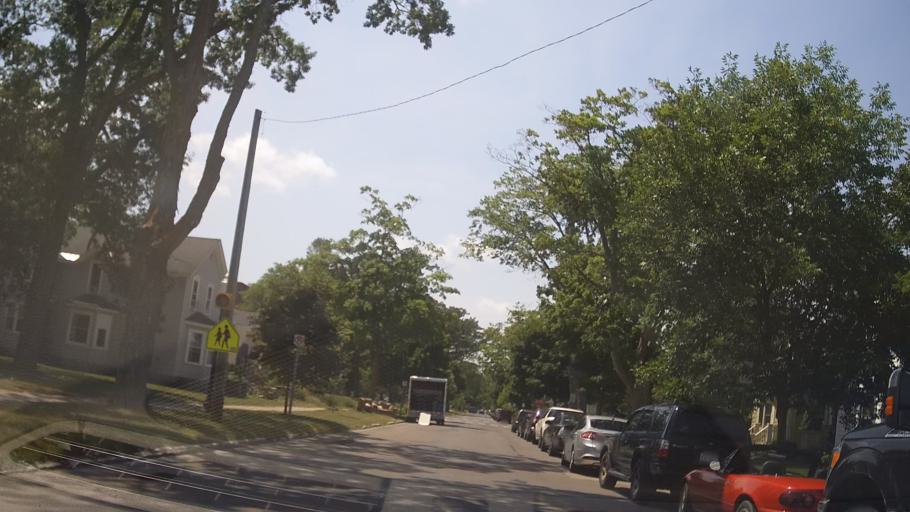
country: US
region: Michigan
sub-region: Grand Traverse County
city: Traverse City
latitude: 44.7605
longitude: -85.6249
